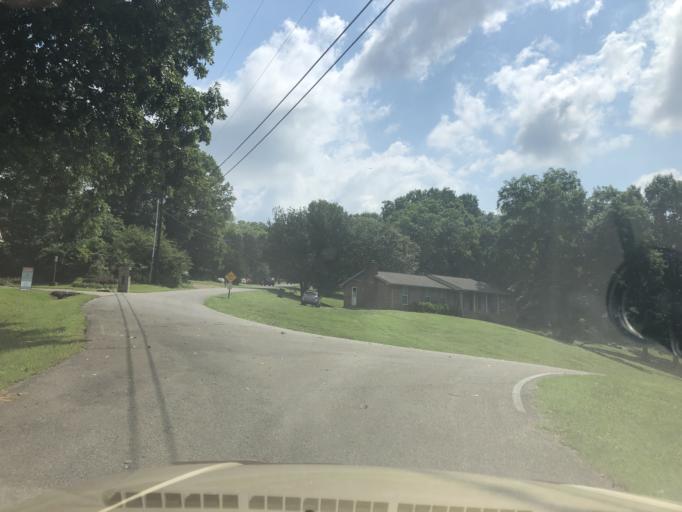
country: US
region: Tennessee
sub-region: Wilson County
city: Green Hill
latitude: 36.2445
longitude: -86.5897
